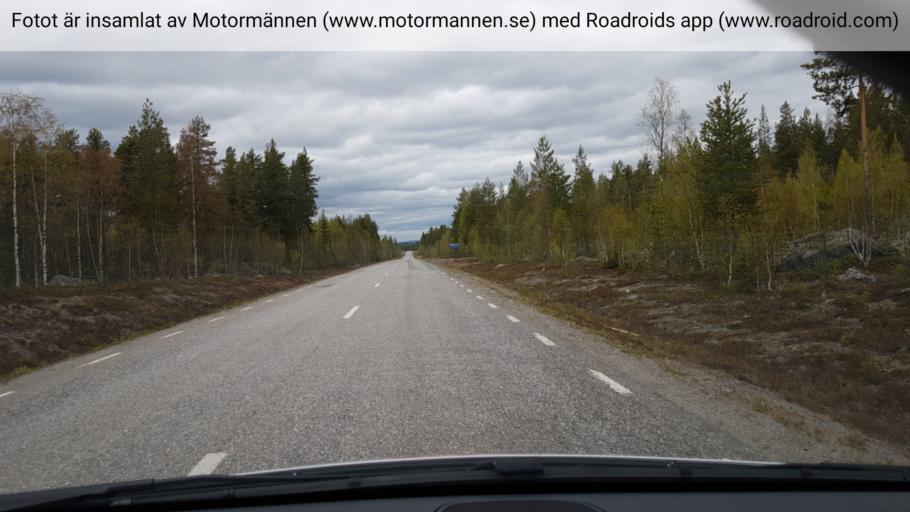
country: SE
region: Vaesterbotten
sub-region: Lycksele Kommun
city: Soderfors
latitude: 65.2597
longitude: 18.0603
